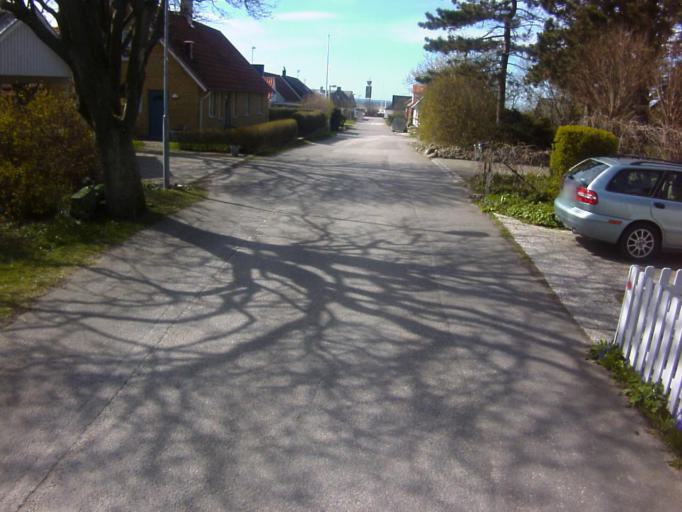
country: SE
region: Skane
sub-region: Kavlinge Kommun
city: Hofterup
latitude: 55.7568
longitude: 12.9079
